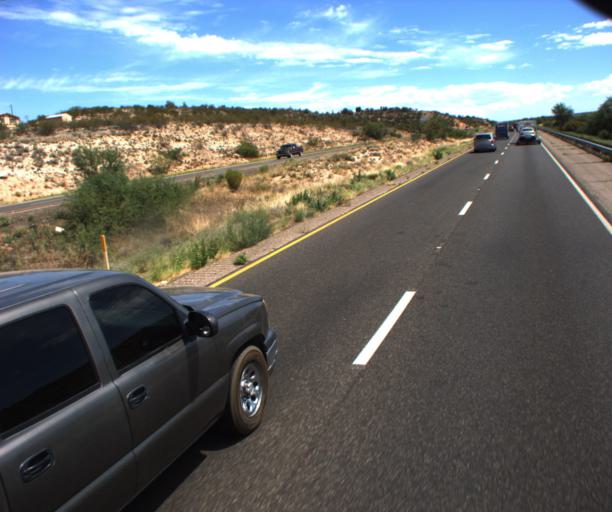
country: US
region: Arizona
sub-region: Yavapai County
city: Lake Montezuma
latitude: 34.6453
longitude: -111.8053
